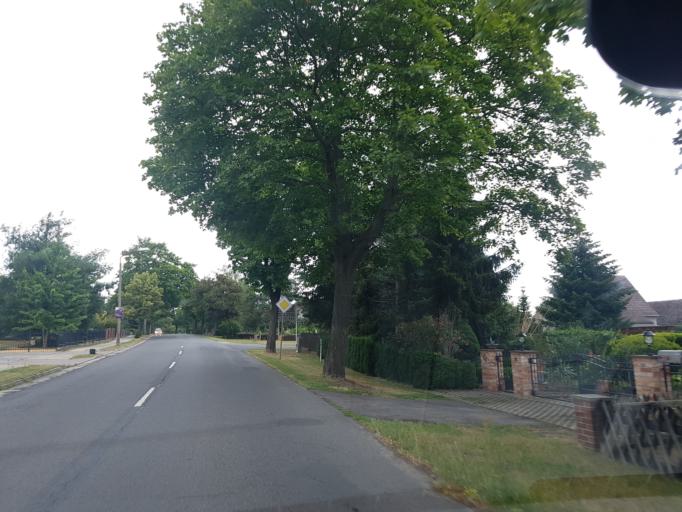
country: DE
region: Brandenburg
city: Luckau
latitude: 51.8436
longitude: 13.6975
